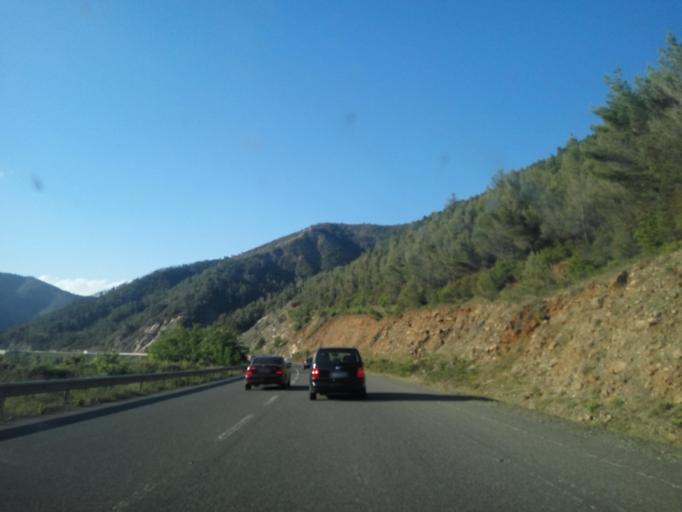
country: AL
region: Lezhe
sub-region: Rrethi i Mirdites
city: Rubik
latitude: 41.7696
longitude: 19.7896
